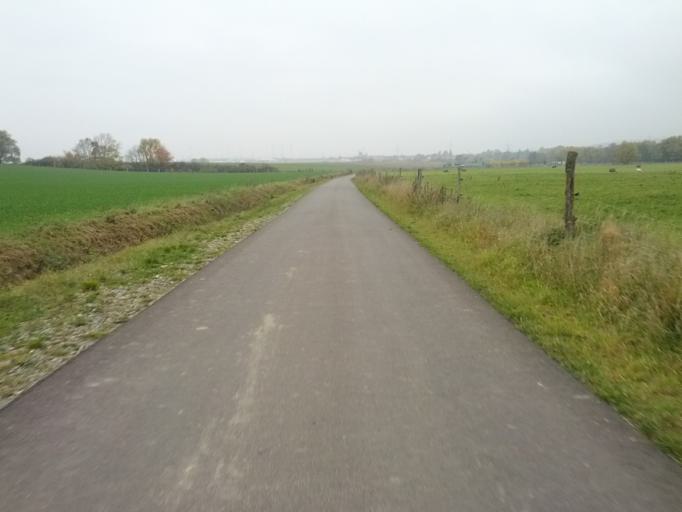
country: DE
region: Thuringia
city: Seebach
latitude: 50.9803
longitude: 10.4183
